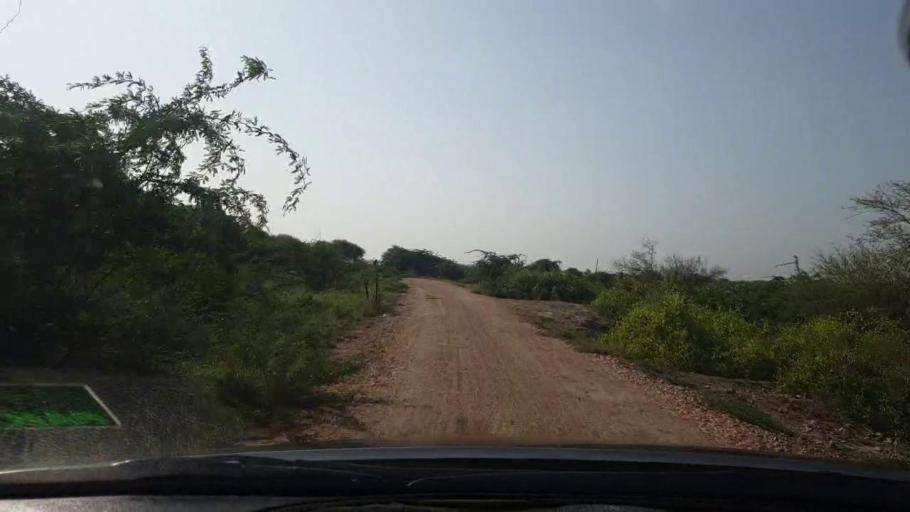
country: PK
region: Sindh
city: Tando Bago
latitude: 24.7136
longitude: 68.9782
